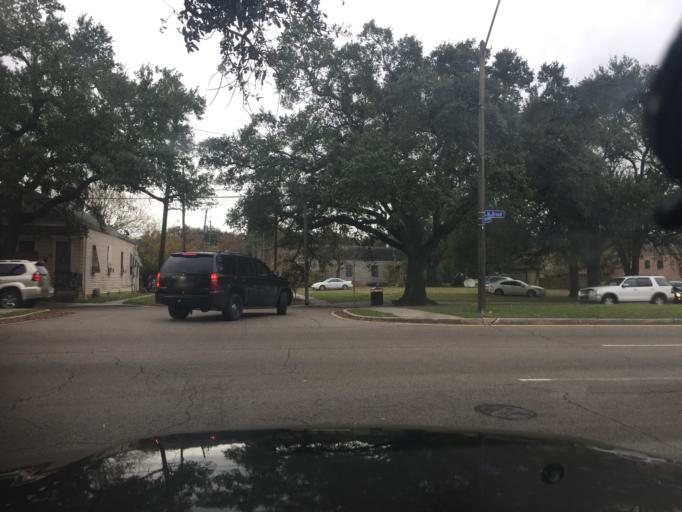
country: US
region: Louisiana
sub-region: Orleans Parish
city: New Orleans
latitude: 29.9794
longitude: -90.0755
